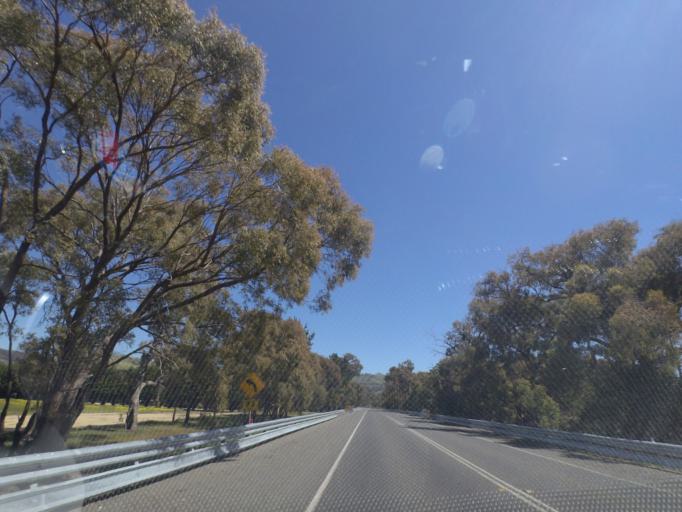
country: AU
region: Victoria
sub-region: Hume
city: Sunbury
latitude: -37.3008
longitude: 144.8270
